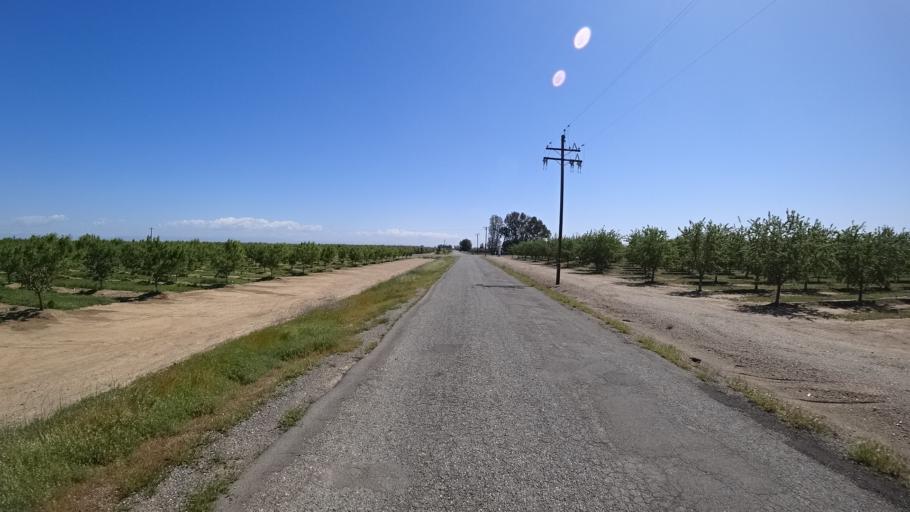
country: US
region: California
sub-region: Glenn County
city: Orland
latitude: 39.6815
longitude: -122.1418
